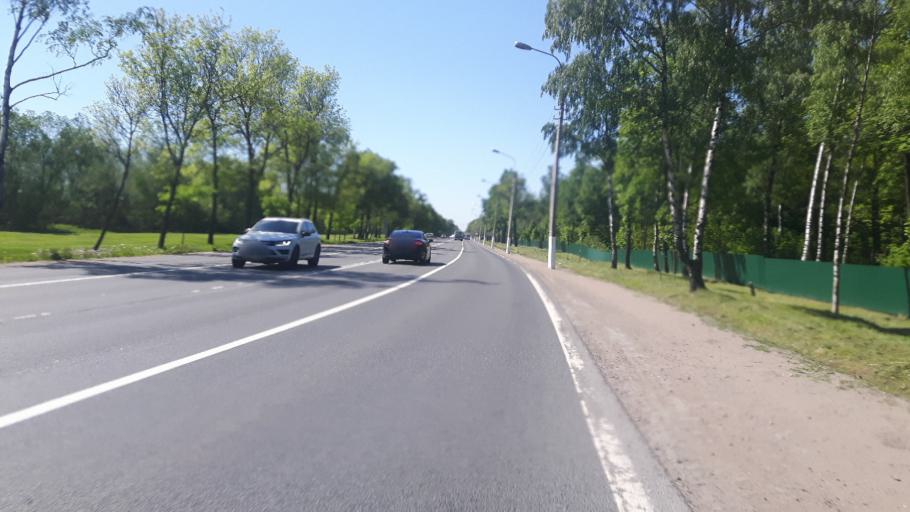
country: RU
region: Leningrad
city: Gorbunki
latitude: 59.8715
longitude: 29.9683
